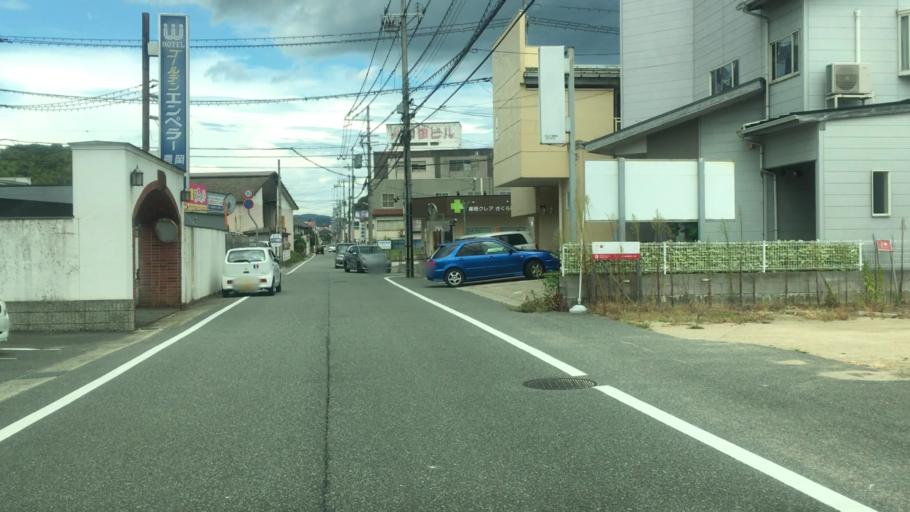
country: JP
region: Hyogo
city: Toyooka
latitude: 35.5329
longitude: 134.8208
